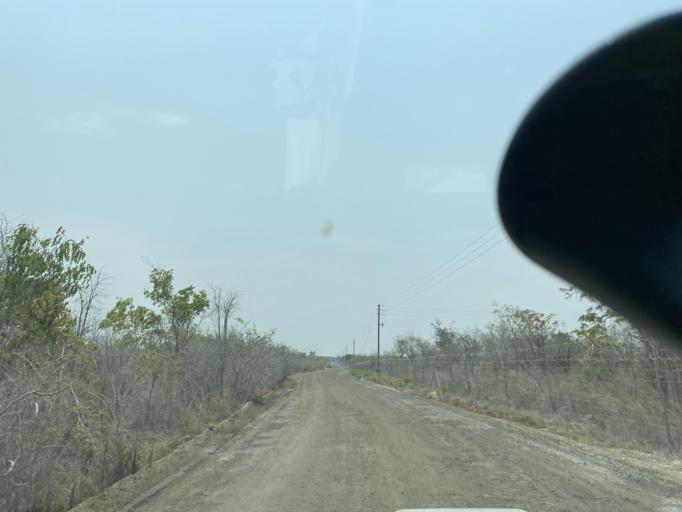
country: ZM
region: Lusaka
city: Lusaka
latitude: -15.5319
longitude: 28.4475
